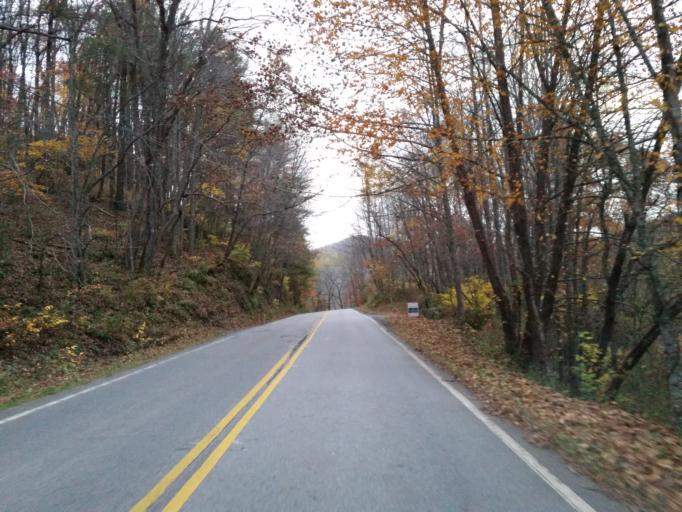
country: US
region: Georgia
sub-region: Union County
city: Blairsville
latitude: 34.7299
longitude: -84.0814
